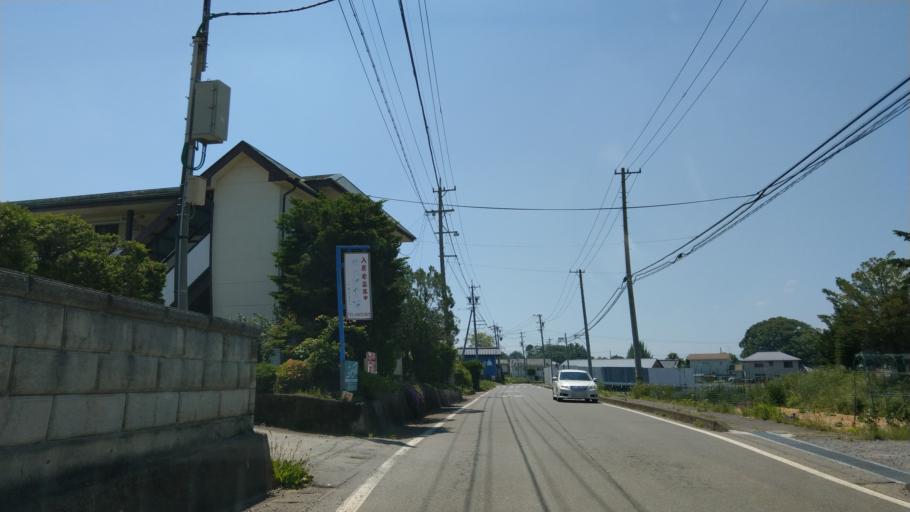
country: JP
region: Nagano
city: Komoro
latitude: 36.2872
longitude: 138.4421
